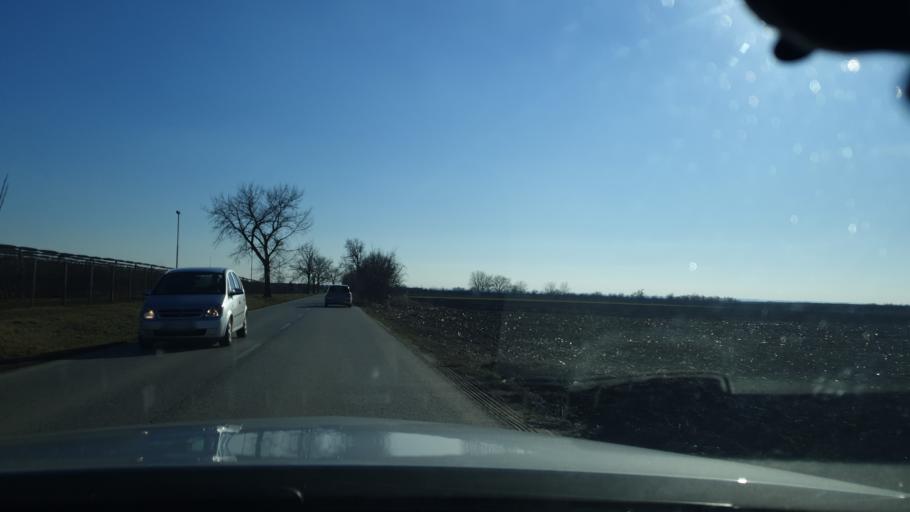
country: RS
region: Autonomna Pokrajina Vojvodina
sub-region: Sremski Okrug
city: Ruma
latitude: 45.0496
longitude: 19.8061
